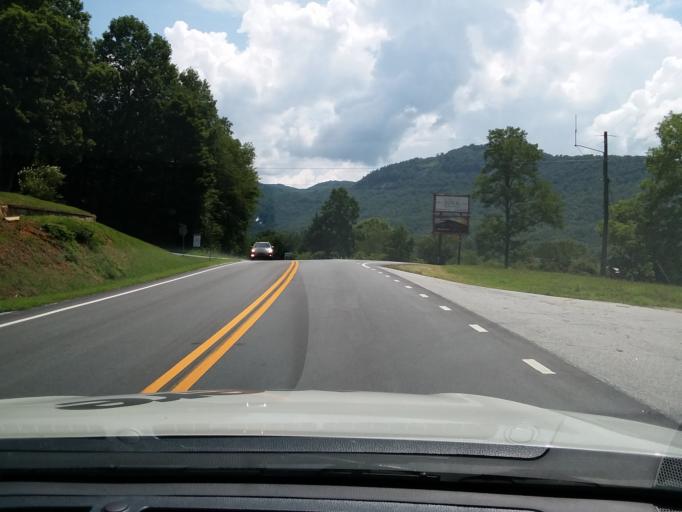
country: US
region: Georgia
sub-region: Rabun County
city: Mountain City
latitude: 34.9858
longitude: -83.3708
